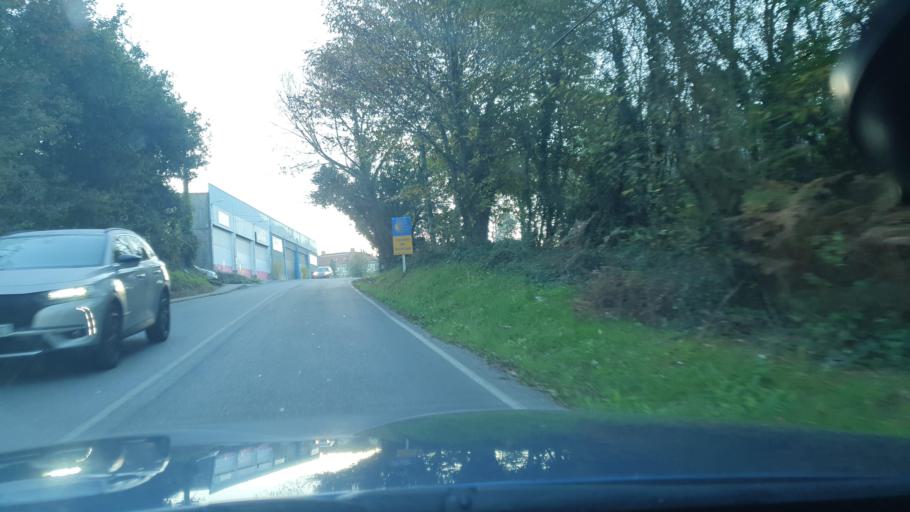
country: ES
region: Galicia
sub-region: Provincia da Coruna
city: Santiago de Compostela
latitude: 42.8438
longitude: -8.5835
